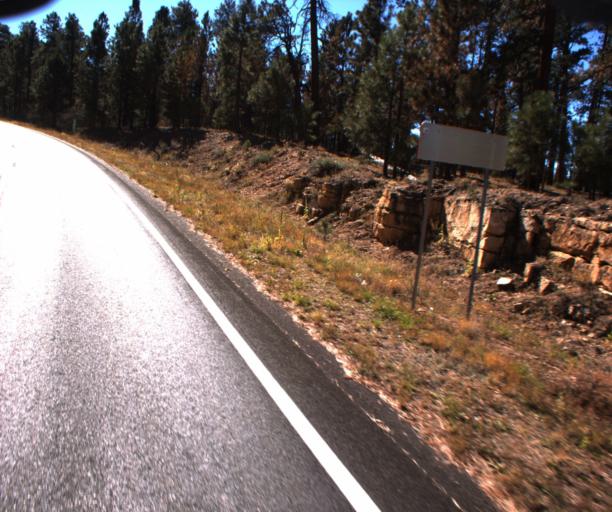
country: US
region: Arizona
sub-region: Coconino County
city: Fredonia
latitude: 36.7051
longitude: -112.2193
